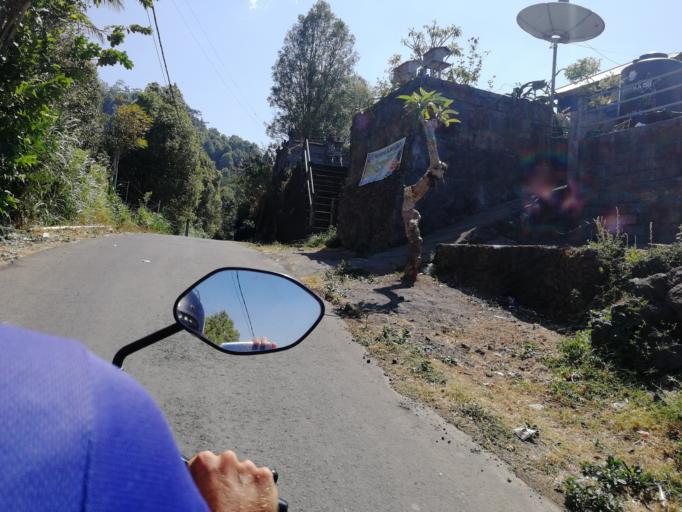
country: ID
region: Bali
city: Banjar Kedisan
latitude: -8.1670
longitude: 115.3028
